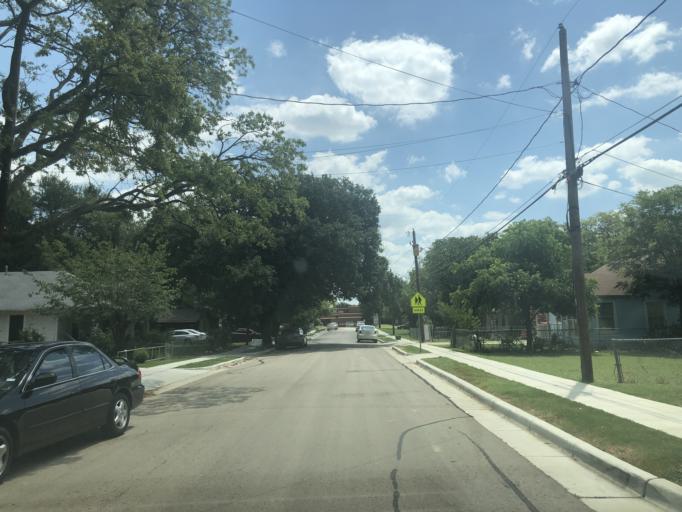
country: US
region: Texas
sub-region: Dallas County
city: Grand Prairie
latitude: 32.7331
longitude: -97.0325
